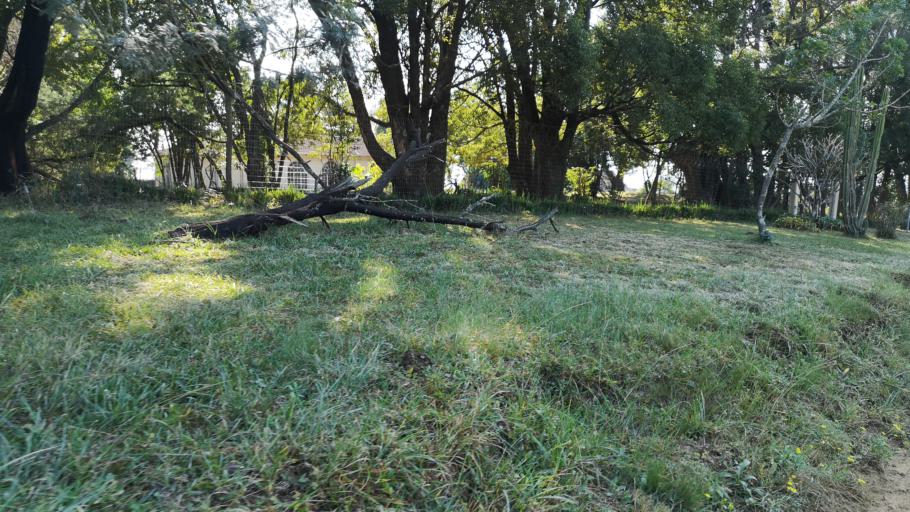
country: ZA
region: KwaZulu-Natal
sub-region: eThekwini Metropolitan Municipality
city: Mpumalanga
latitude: -29.7368
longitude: 30.6825
